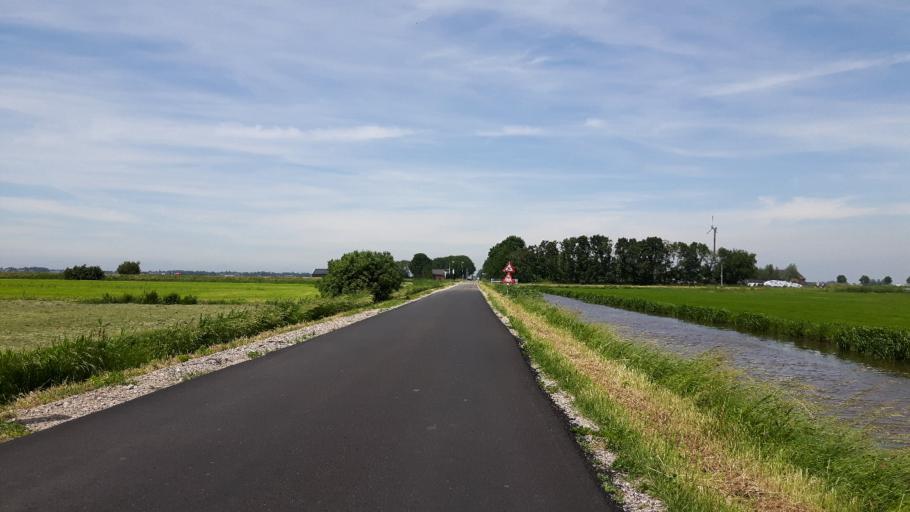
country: NL
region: South Holland
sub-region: Gemeente Nieuwkoop
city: Nieuwkoop
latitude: 52.1423
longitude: 4.7547
